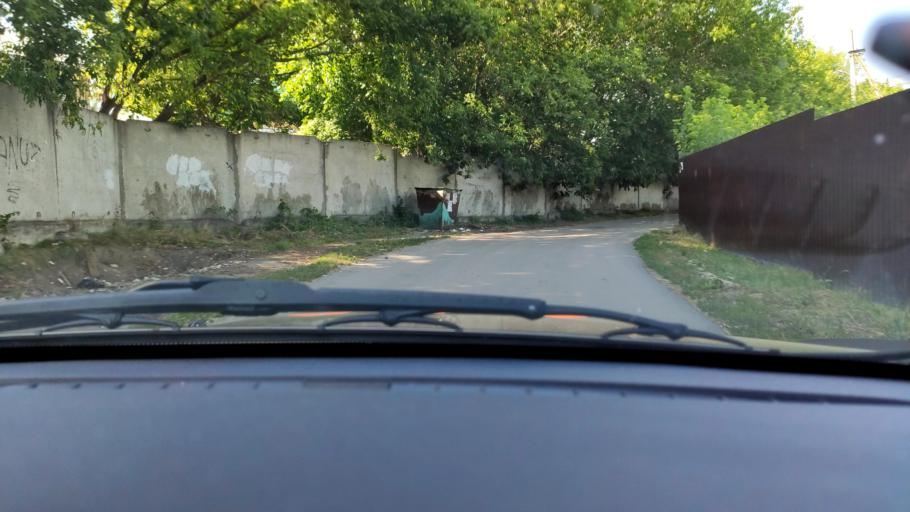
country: RU
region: Voronezj
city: Ramon'
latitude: 51.8240
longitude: 39.2701
